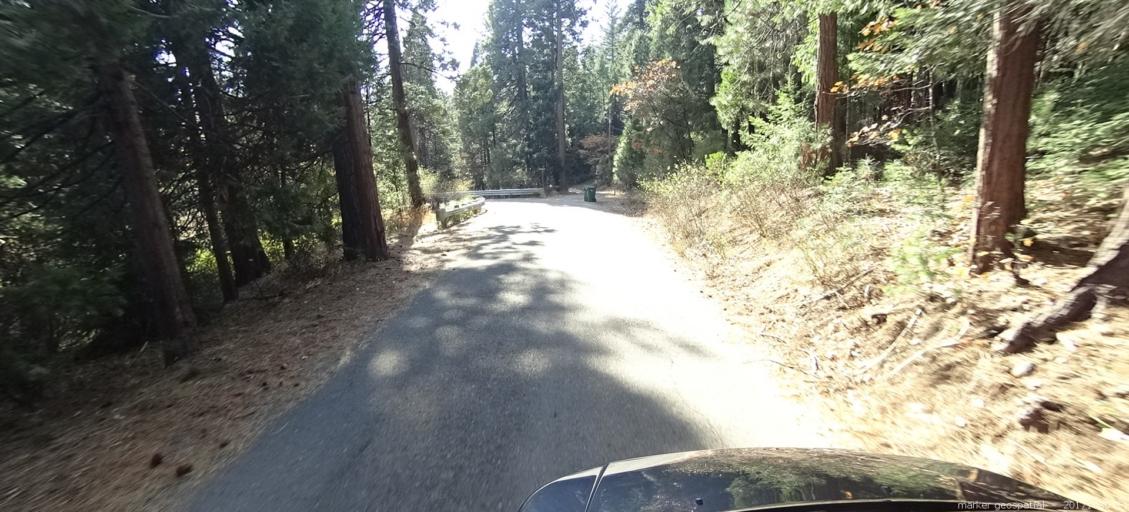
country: US
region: California
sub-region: Shasta County
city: Shingletown
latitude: 40.5033
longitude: -121.7418
